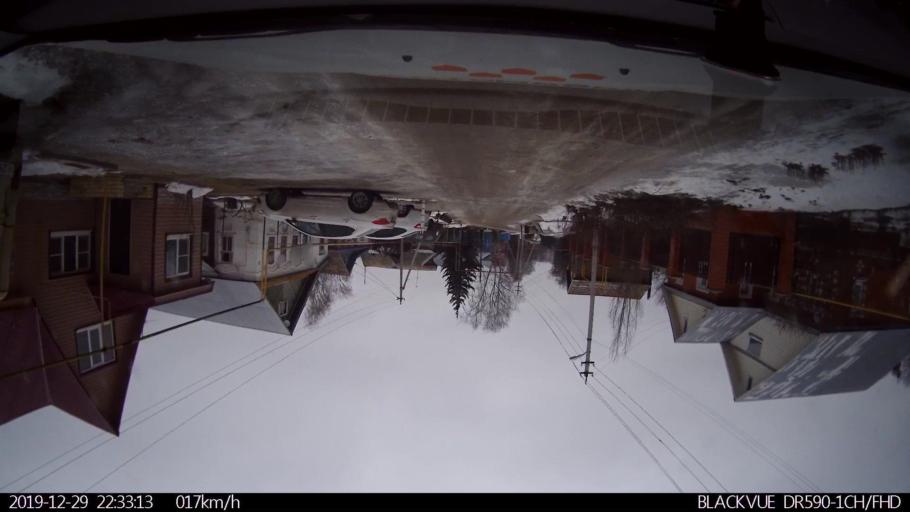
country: RU
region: Nizjnij Novgorod
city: Afonino
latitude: 56.2022
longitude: 43.9858
